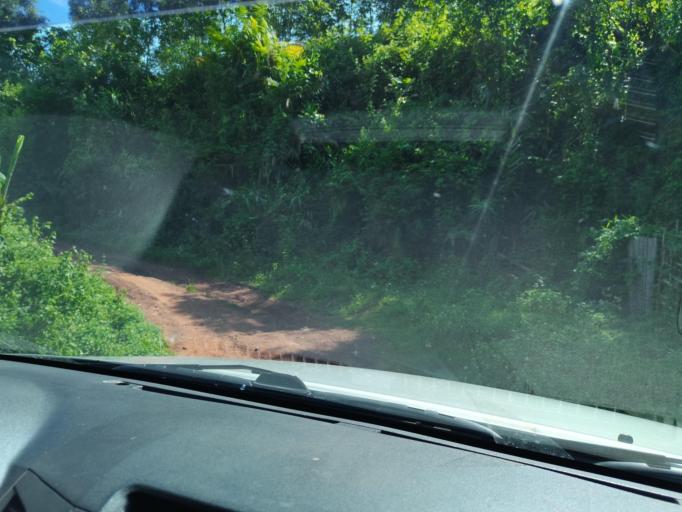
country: LA
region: Loungnamtha
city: Muang Nale
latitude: 20.5571
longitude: 101.0615
